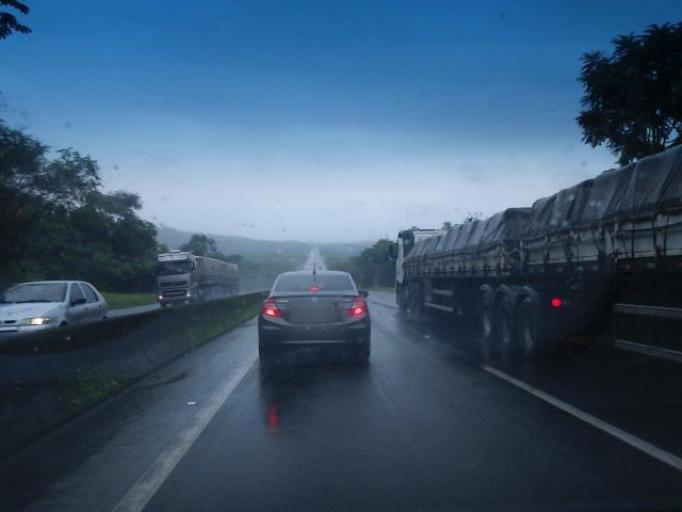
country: BR
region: Santa Catarina
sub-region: Joinville
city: Joinville
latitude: -26.0860
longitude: -48.8621
